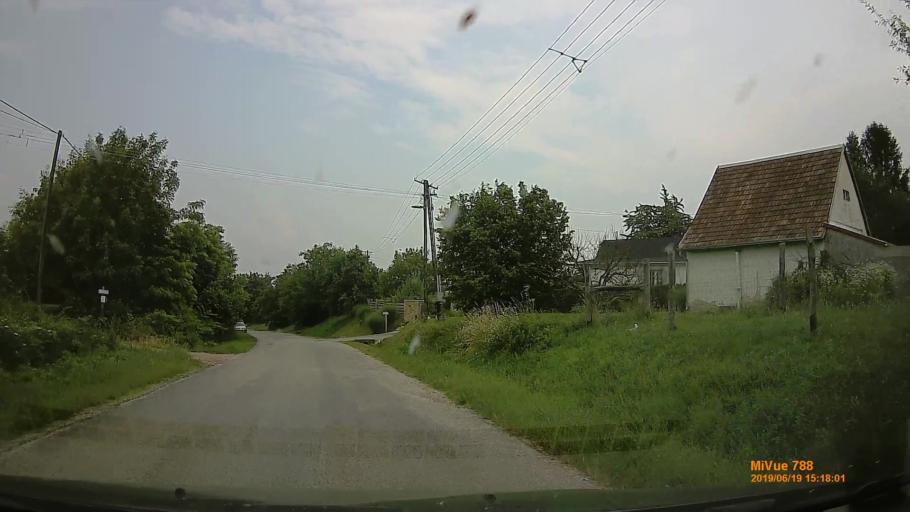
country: HU
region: Baranya
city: Szigetvar
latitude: 46.0778
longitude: 17.8517
